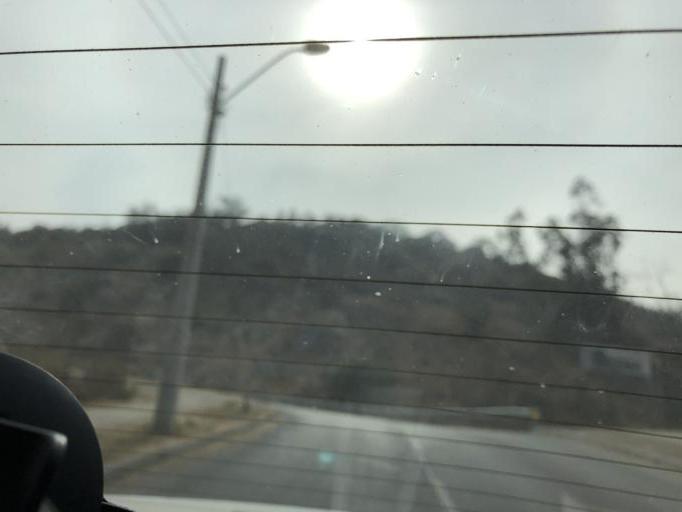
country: CL
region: Santiago Metropolitan
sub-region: Provincia de Cordillera
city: Puente Alto
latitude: -33.5552
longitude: -70.5475
